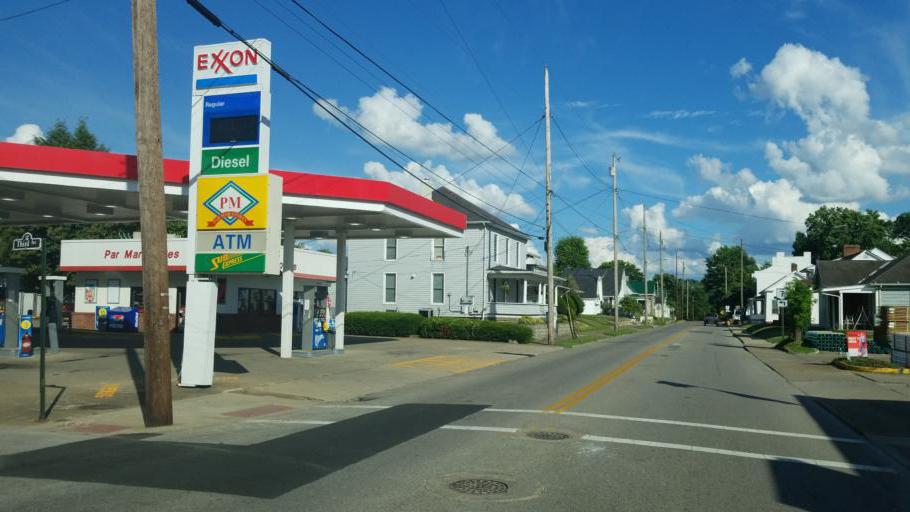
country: US
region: Ohio
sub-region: Gallia County
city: Gallipolis
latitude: 38.8048
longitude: -82.2124
